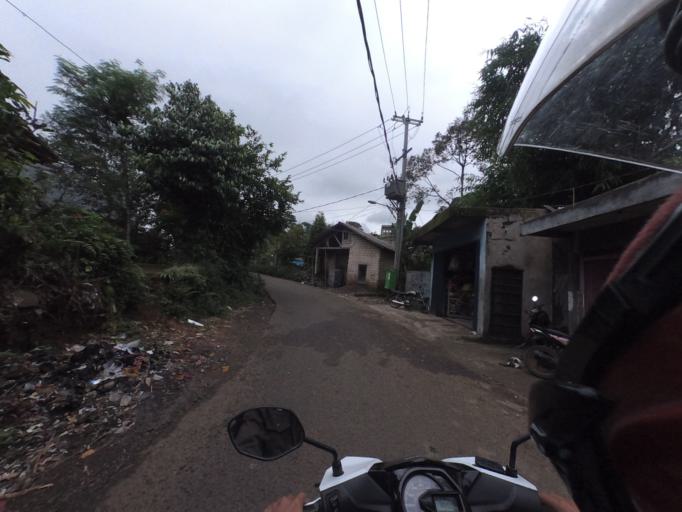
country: ID
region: West Java
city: Bogor
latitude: -6.6357
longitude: 106.7289
